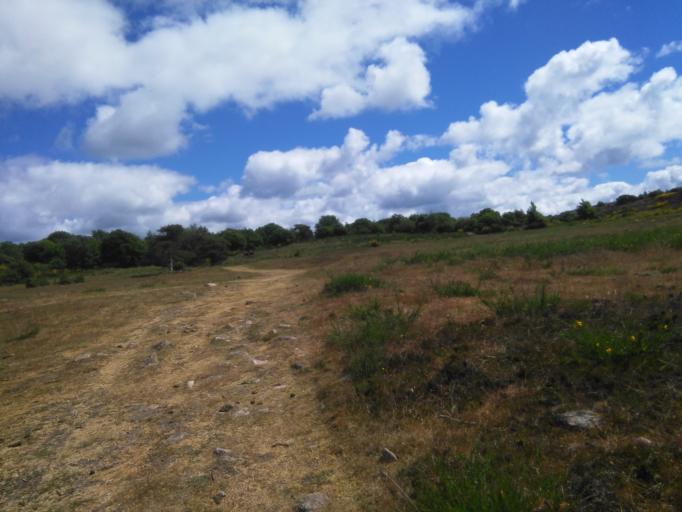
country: DK
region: Capital Region
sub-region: Bornholm Kommune
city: Ronne
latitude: 55.2932
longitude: 14.7664
